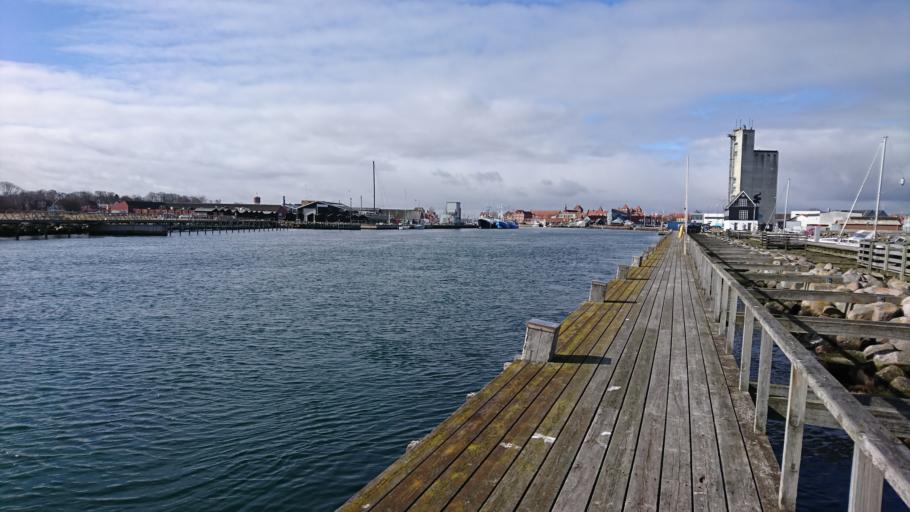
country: DK
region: South Denmark
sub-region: Kerteminde Kommune
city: Kerteminde
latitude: 55.4511
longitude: 10.6678
